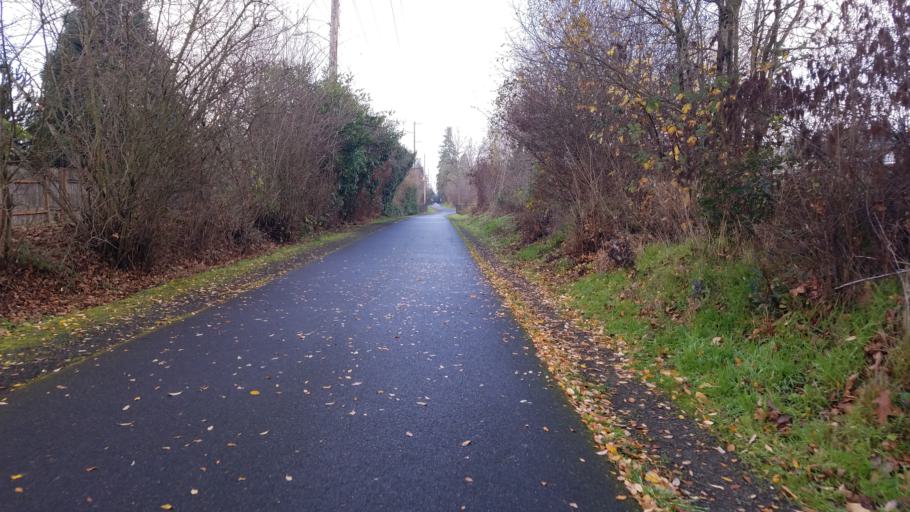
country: US
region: Oregon
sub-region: Clackamas County
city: Jennings Lodge
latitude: 45.3998
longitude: -122.6255
